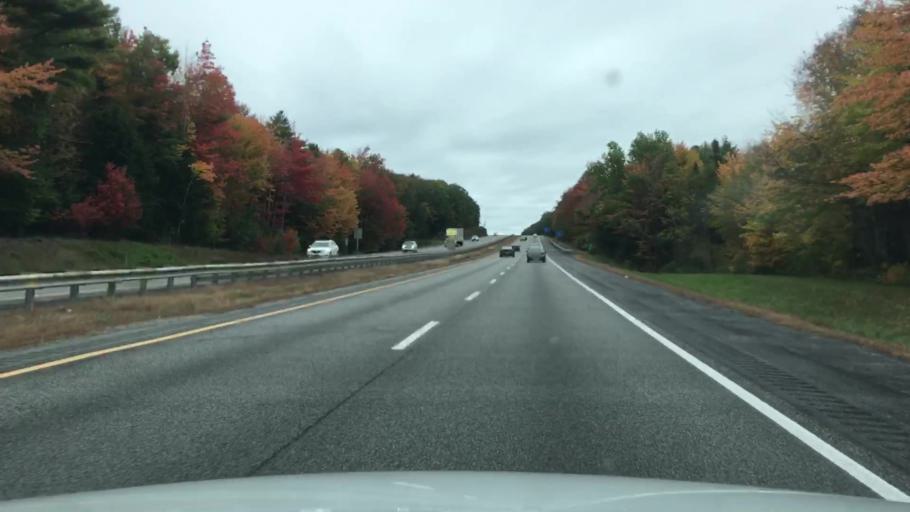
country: US
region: Maine
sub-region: Cumberland County
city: Freeport
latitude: 43.9038
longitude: -70.0647
